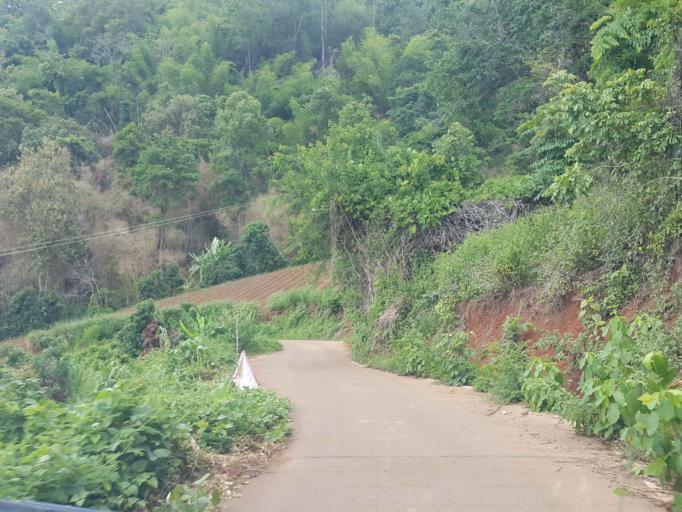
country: TH
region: Chiang Mai
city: Samoeng
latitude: 18.7813
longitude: 98.8307
